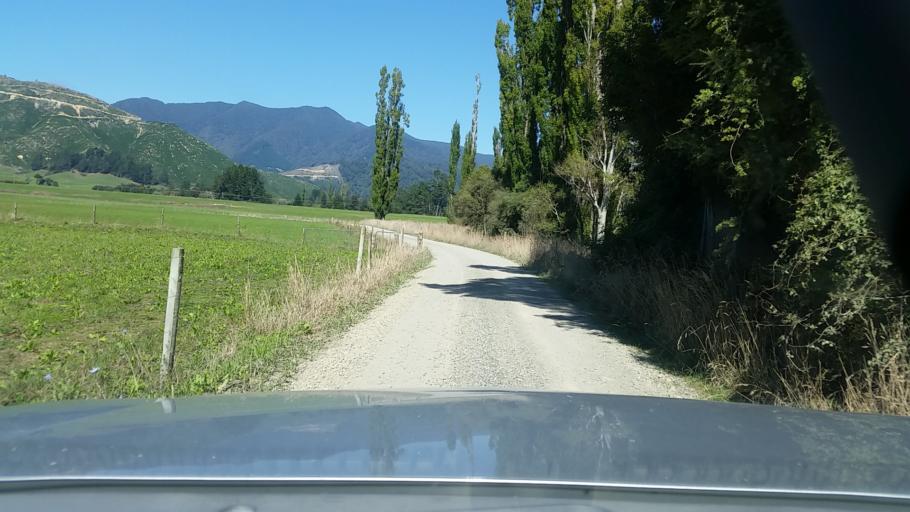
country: NZ
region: Nelson
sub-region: Nelson City
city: Nelson
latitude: -41.2681
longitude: 173.5756
